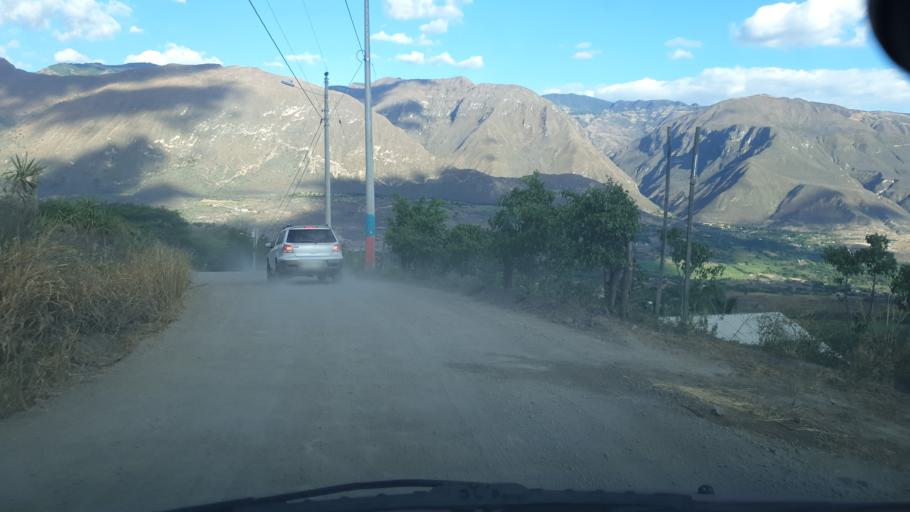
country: EC
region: Azuay
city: Cuenca
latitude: -3.2853
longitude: -79.2963
